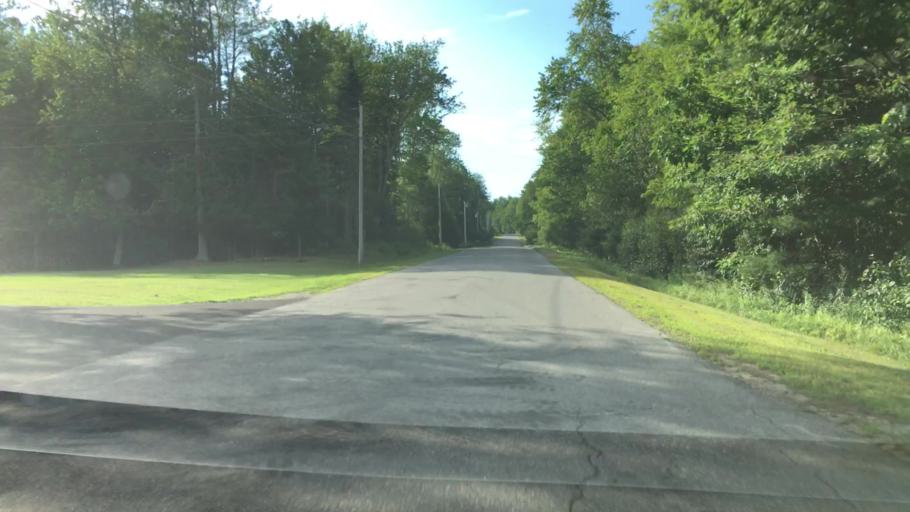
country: US
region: Maine
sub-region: Waldo County
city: Stockton Springs
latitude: 44.4894
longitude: -68.8656
